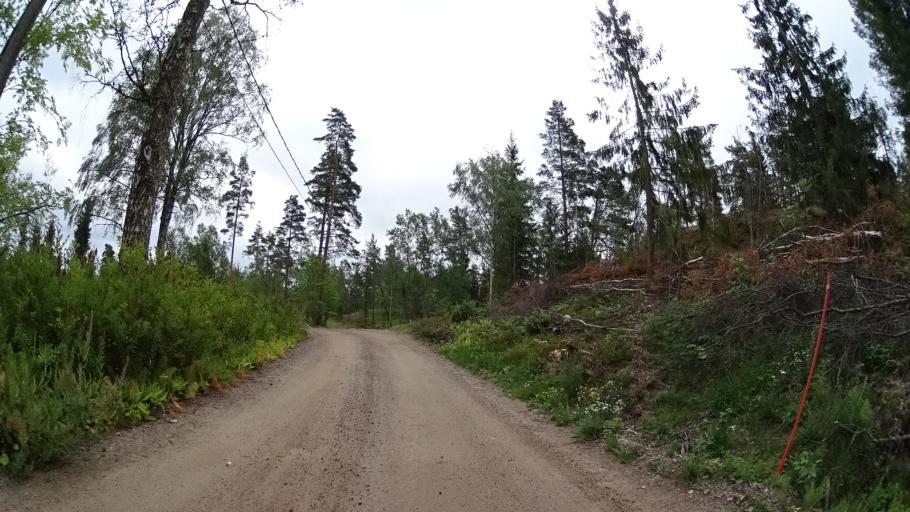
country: FI
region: Uusimaa
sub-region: Helsinki
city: Kauniainen
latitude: 60.1999
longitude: 24.7324
